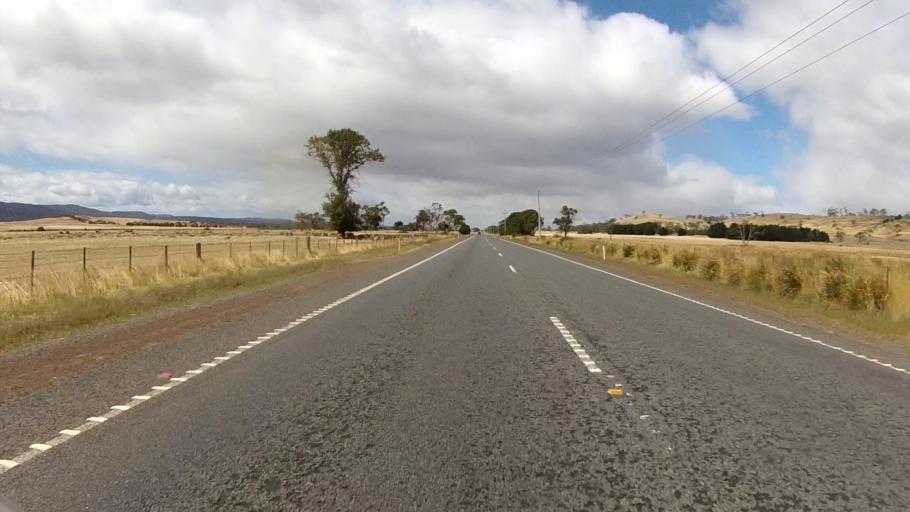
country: AU
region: Tasmania
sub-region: Northern Midlands
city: Evandale
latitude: -41.9603
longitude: 147.4981
